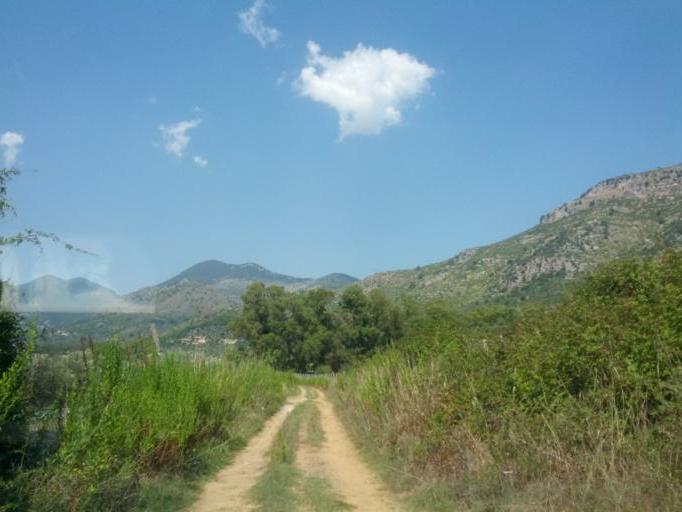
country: IT
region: Latium
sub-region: Provincia di Latina
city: Monte San Biagio
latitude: 41.3646
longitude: 13.3570
